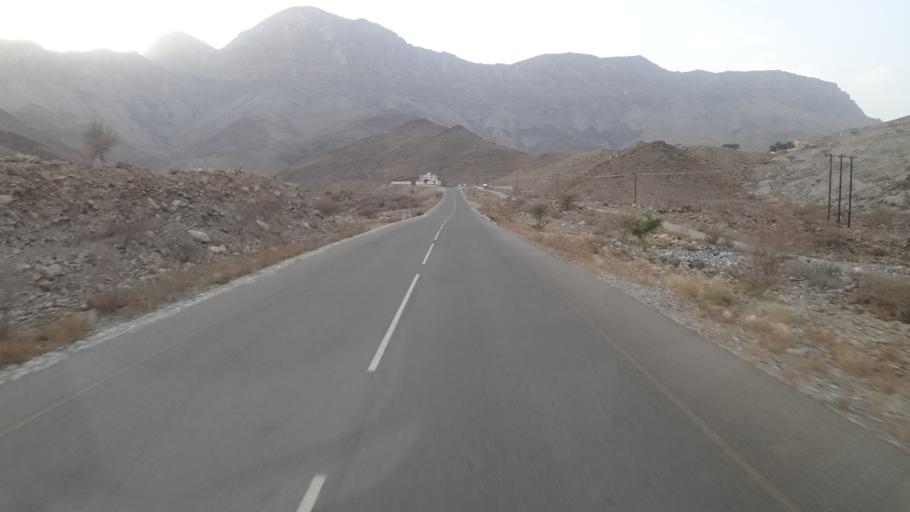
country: OM
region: Muhafazat ad Dakhiliyah
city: Bahla'
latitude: 23.1792
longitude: 57.1433
